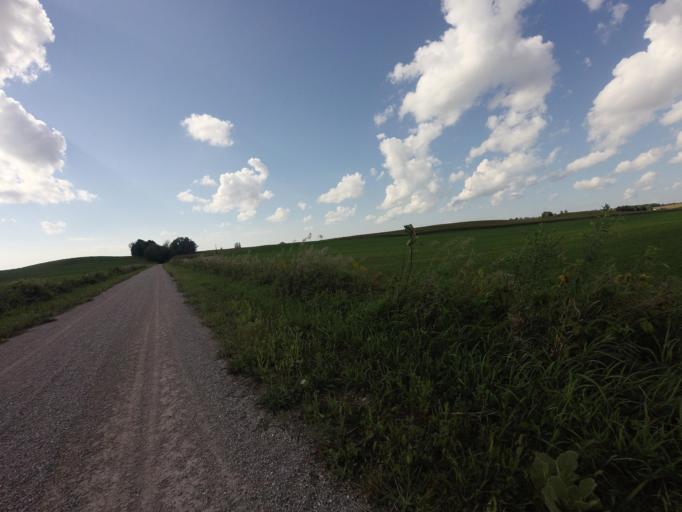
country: CA
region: Ontario
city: Huron East
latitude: 43.7427
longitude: -81.4852
